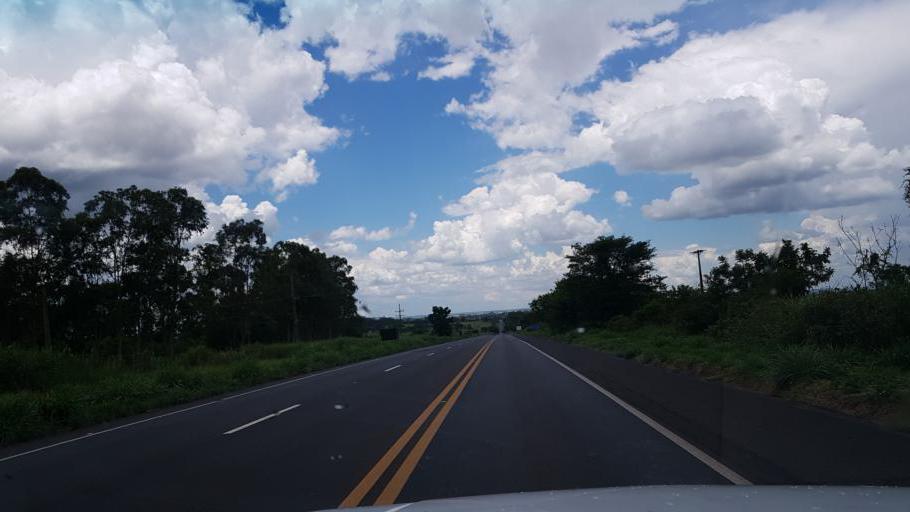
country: BR
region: Sao Paulo
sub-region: Paraguacu Paulista
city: Paraguacu Paulista
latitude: -22.3828
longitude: -50.6170
